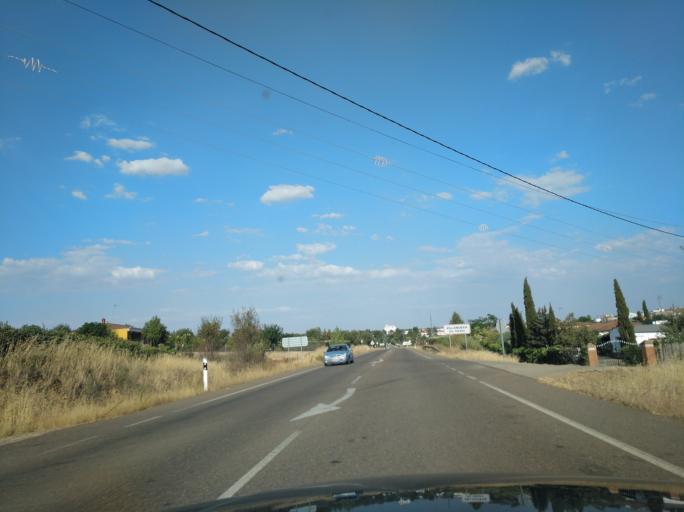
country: ES
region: Extremadura
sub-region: Provincia de Badajoz
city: Villanueva del Fresno
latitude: 38.3774
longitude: -7.1749
